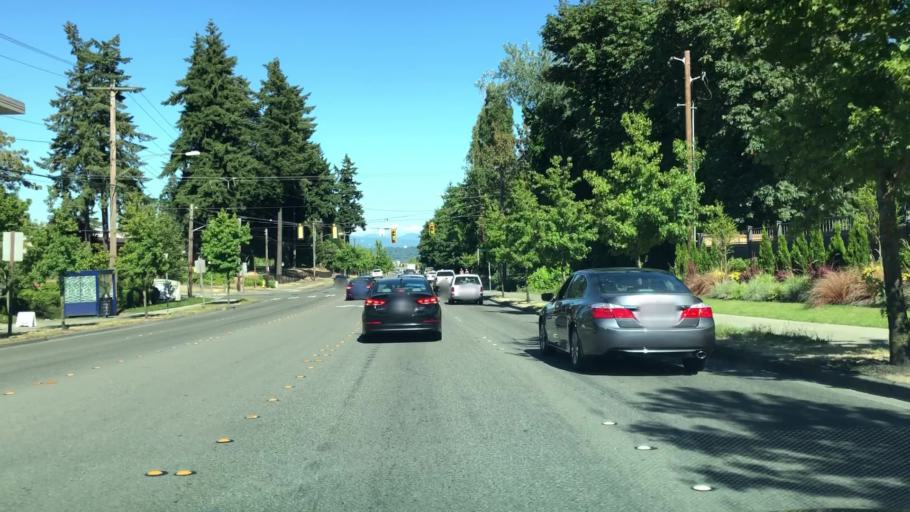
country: US
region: Washington
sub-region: King County
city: SeaTac
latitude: 47.4344
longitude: -122.2828
